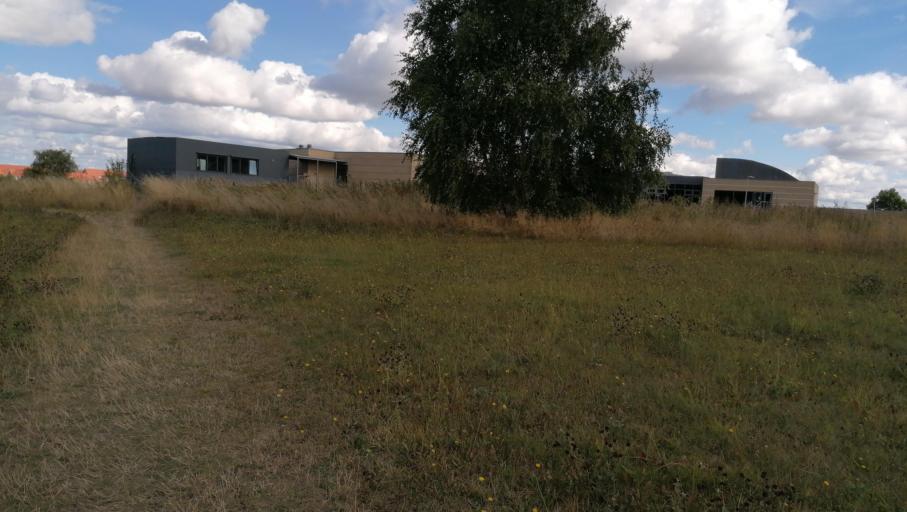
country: DK
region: Zealand
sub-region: Holbaek Kommune
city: Holbaek
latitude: 55.7121
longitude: 11.6977
